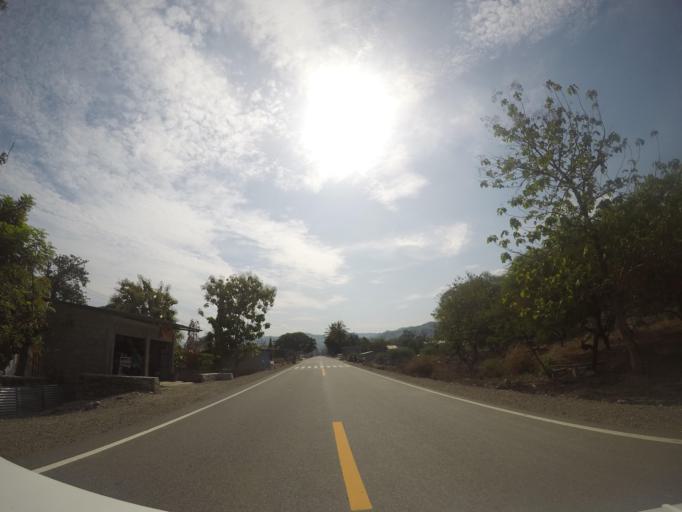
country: ID
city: Metinaro
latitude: -8.5300
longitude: 125.7368
